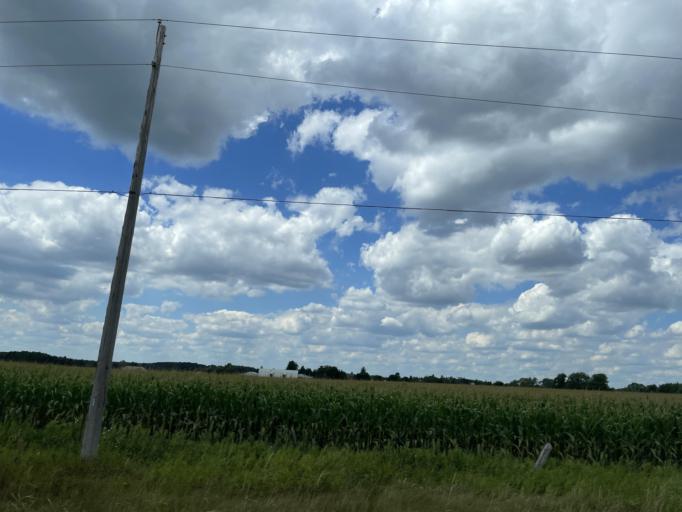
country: CA
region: Ontario
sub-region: Wellington County
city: Guelph
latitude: 43.5426
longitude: -80.3590
